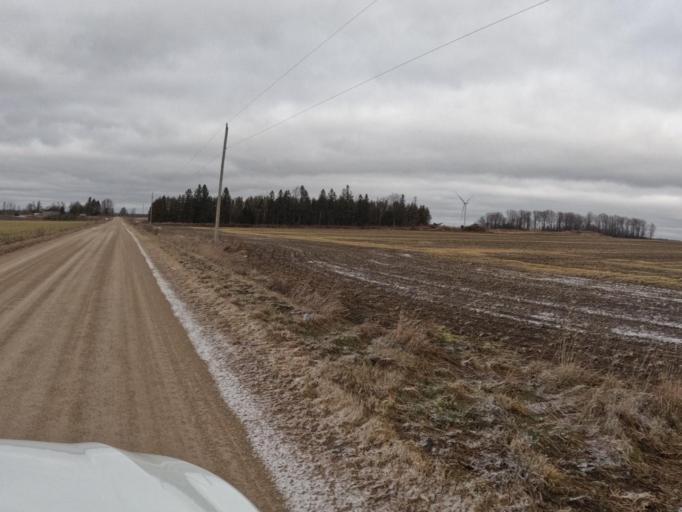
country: CA
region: Ontario
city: Shelburne
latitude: 44.0218
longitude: -80.3693
